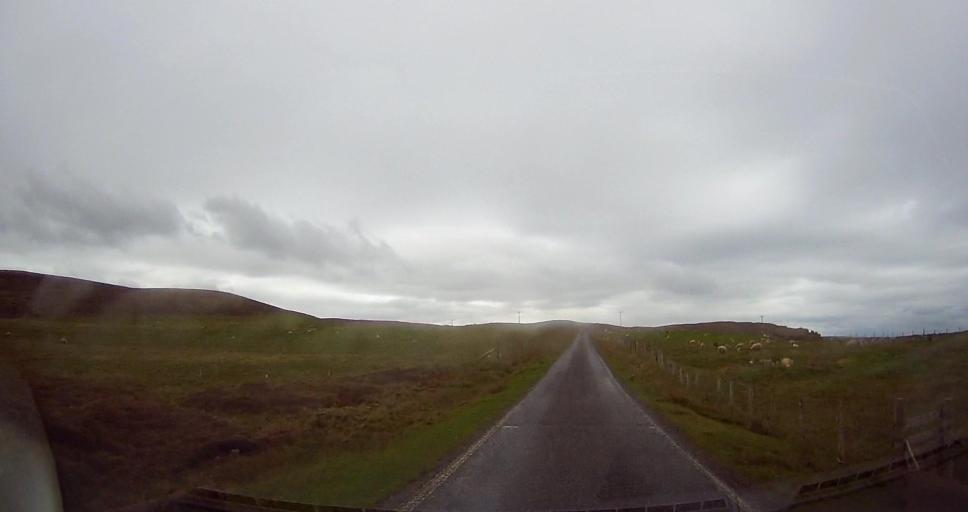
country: GB
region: Scotland
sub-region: Shetland Islands
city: Lerwick
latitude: 60.4943
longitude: -1.5534
